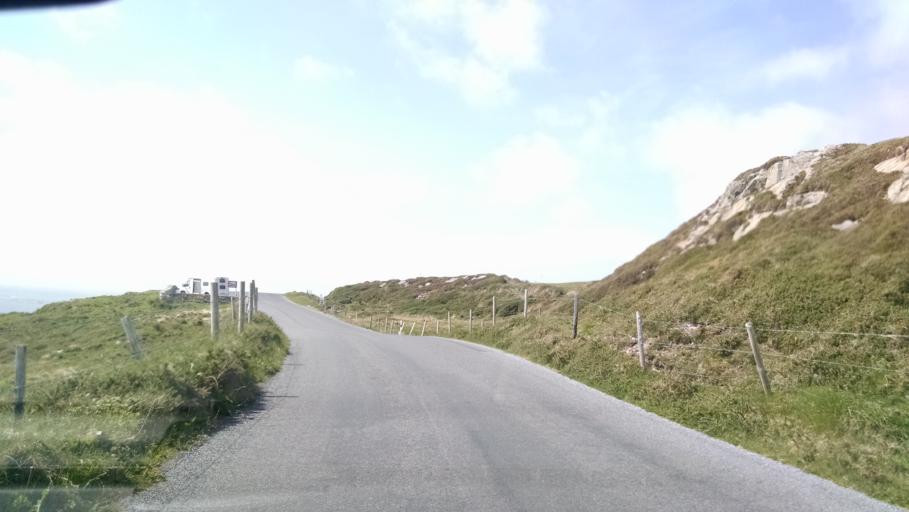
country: IE
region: Connaught
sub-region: County Galway
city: Clifden
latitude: 53.5003
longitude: -10.0950
